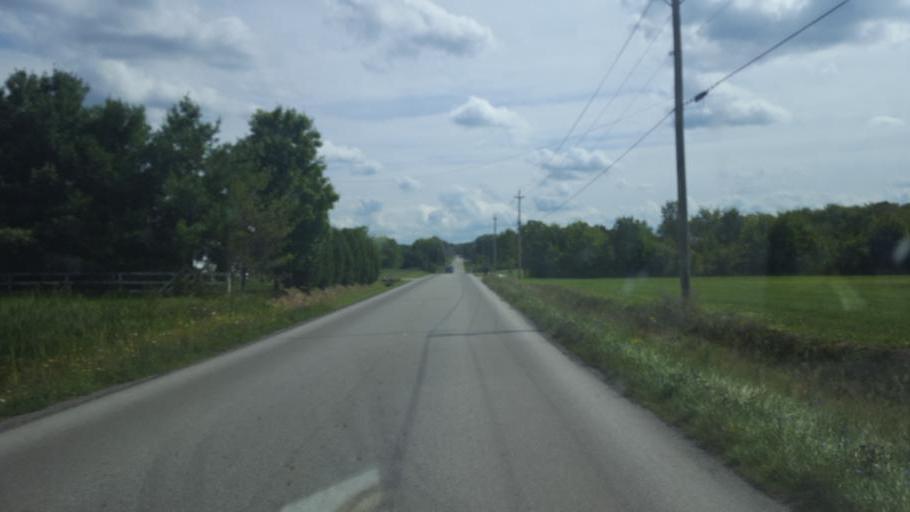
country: US
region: Ohio
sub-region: Geauga County
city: Middlefield
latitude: 41.4259
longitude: -81.0737
